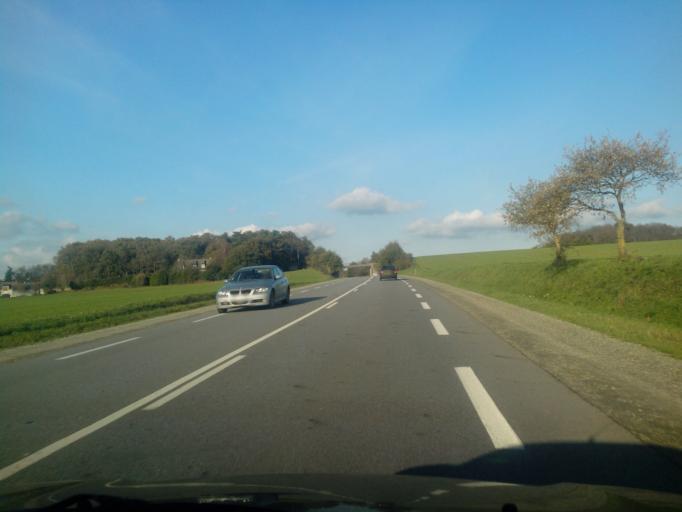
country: FR
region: Brittany
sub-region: Departement du Morbihan
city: Loyat
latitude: 47.9645
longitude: -2.3845
